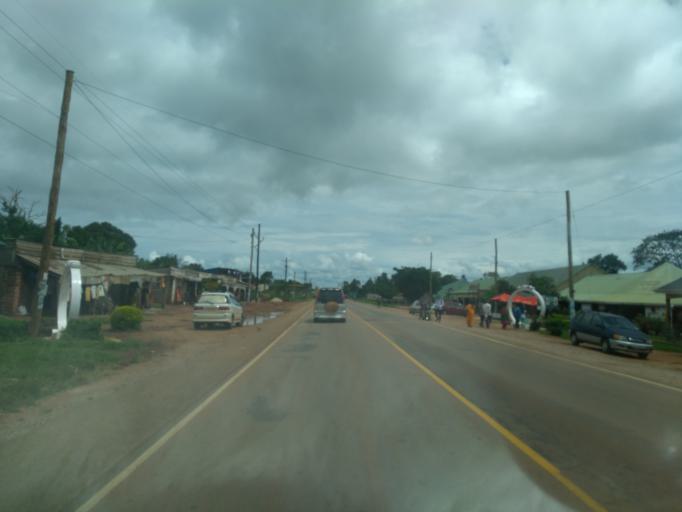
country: UG
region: Central Region
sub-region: Butambala District
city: Gombe
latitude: 0.0004
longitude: 32.0402
